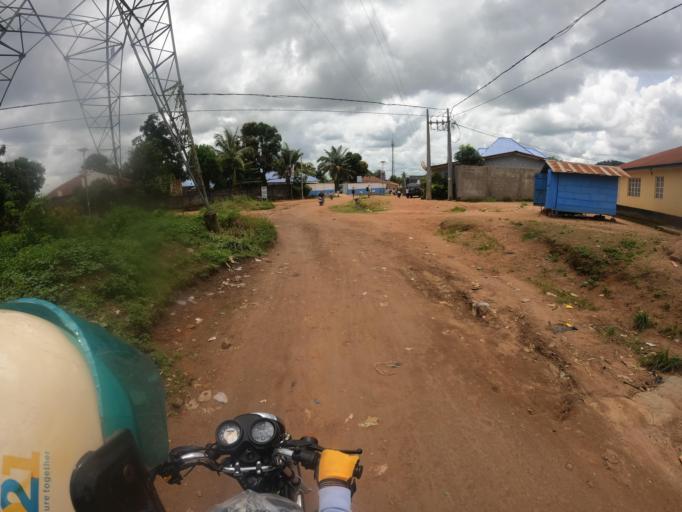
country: SL
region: Northern Province
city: Makeni
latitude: 8.8931
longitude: -12.0492
